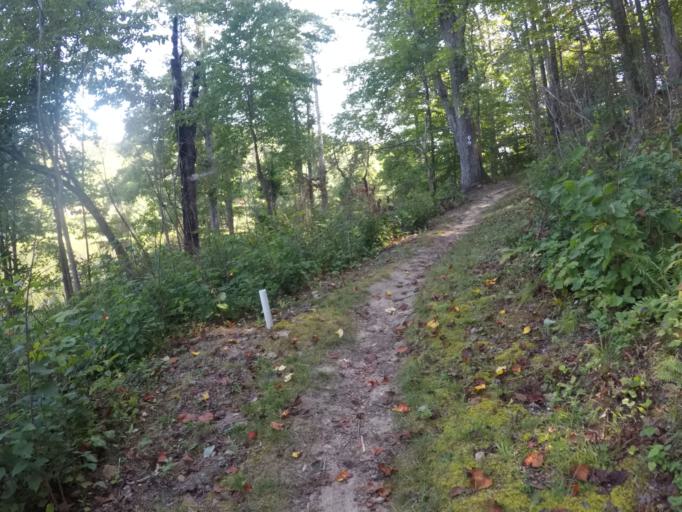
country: US
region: Ohio
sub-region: Lawrence County
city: Ironton
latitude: 38.6183
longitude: -82.6270
